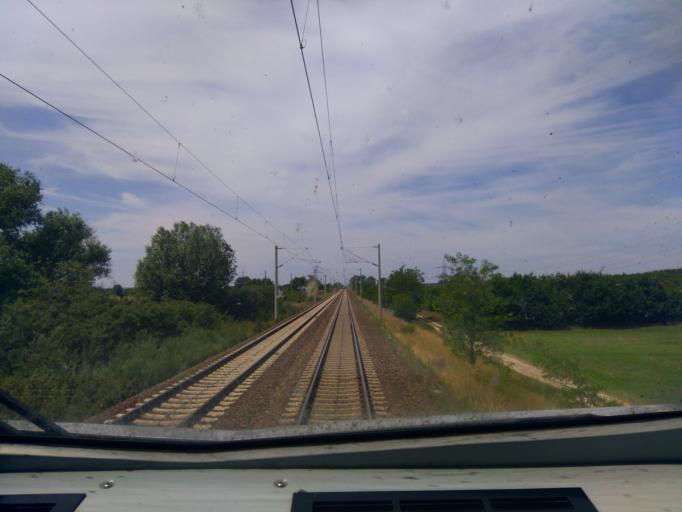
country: DE
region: Brandenburg
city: Wustermark
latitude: 52.5969
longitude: 12.9465
